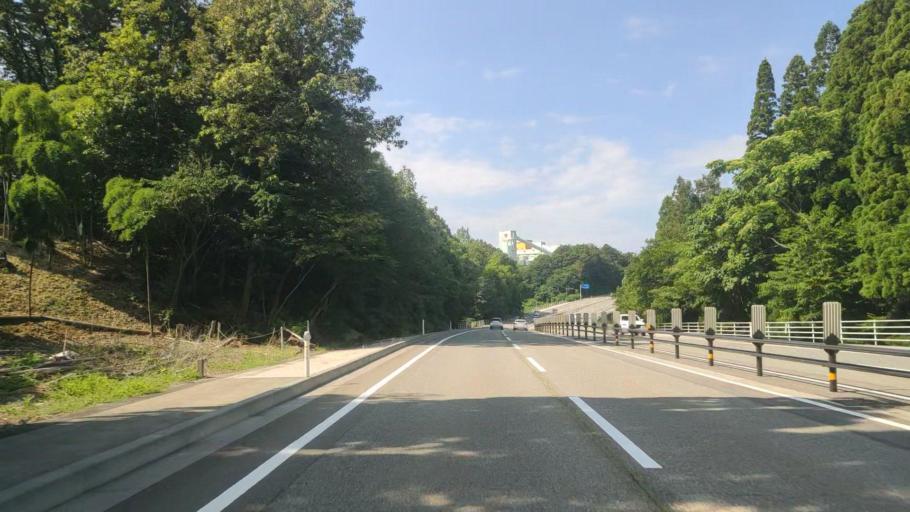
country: JP
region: Ishikawa
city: Komatsu
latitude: 36.4221
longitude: 136.5289
